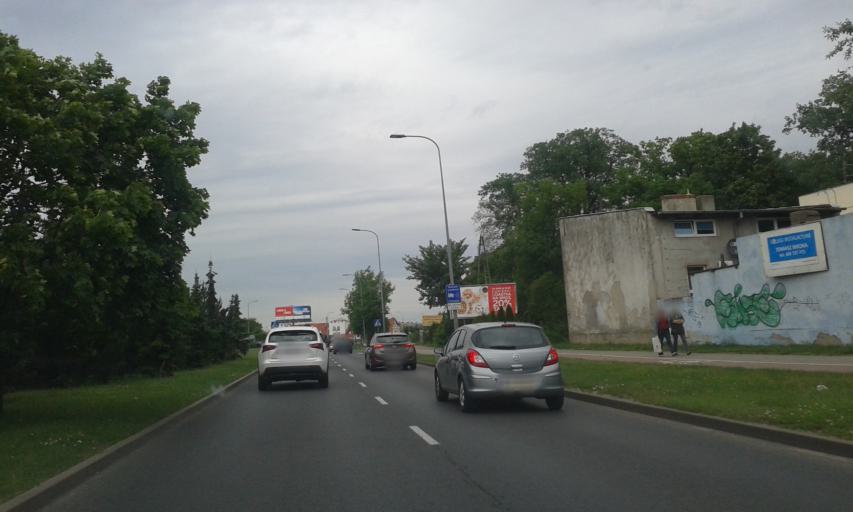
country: PL
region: Kujawsko-Pomorskie
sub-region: Bydgoszcz
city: Bydgoszcz
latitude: 53.1379
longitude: 17.9643
